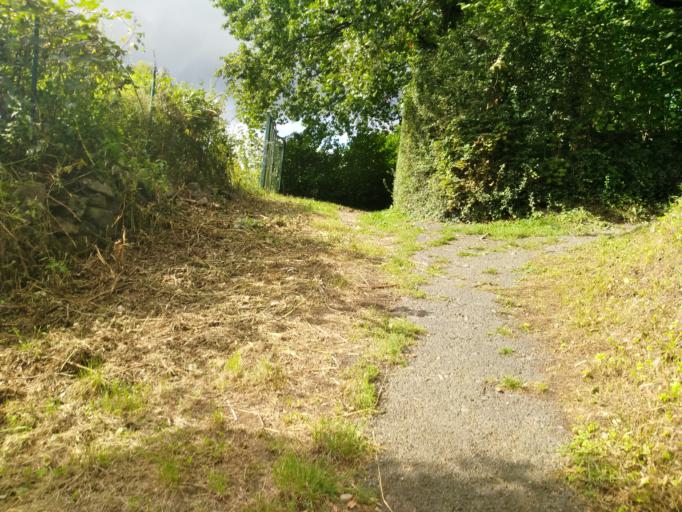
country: DE
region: North Rhine-Westphalia
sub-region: Regierungsbezirk Koln
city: Bad Honnef
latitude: 50.6532
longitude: 7.2259
